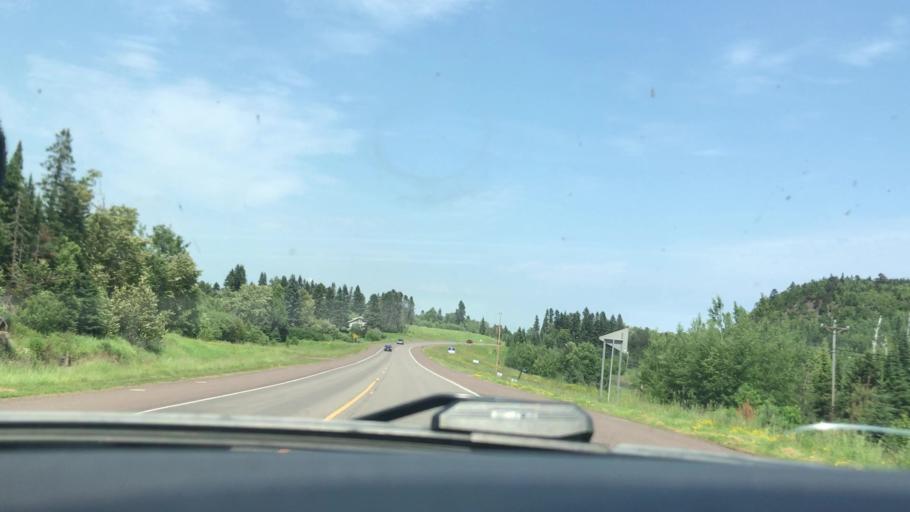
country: US
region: Minnesota
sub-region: Lake County
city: Silver Bay
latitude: 47.3163
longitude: -91.2244
